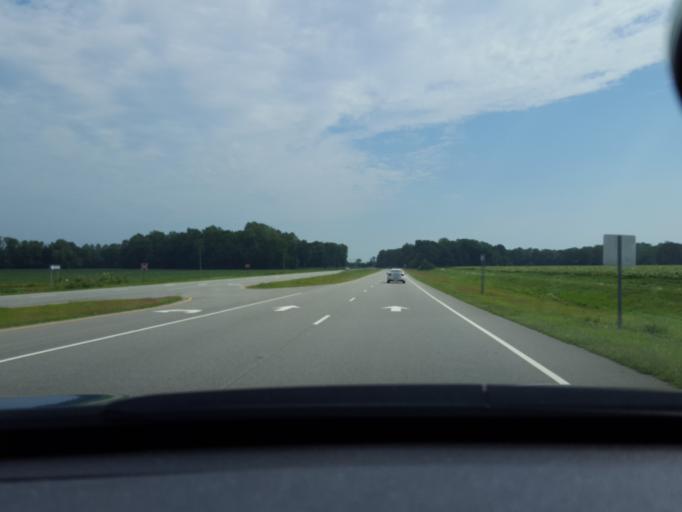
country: US
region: North Carolina
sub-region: Chowan County
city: Edenton
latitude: 36.0364
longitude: -76.7220
